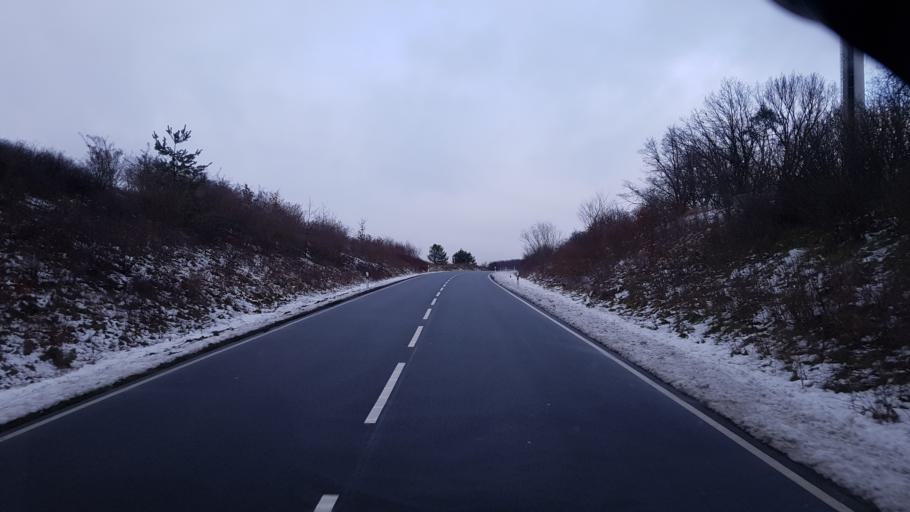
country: DE
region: Brandenburg
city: Heinersbruck
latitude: 51.8398
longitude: 14.5869
